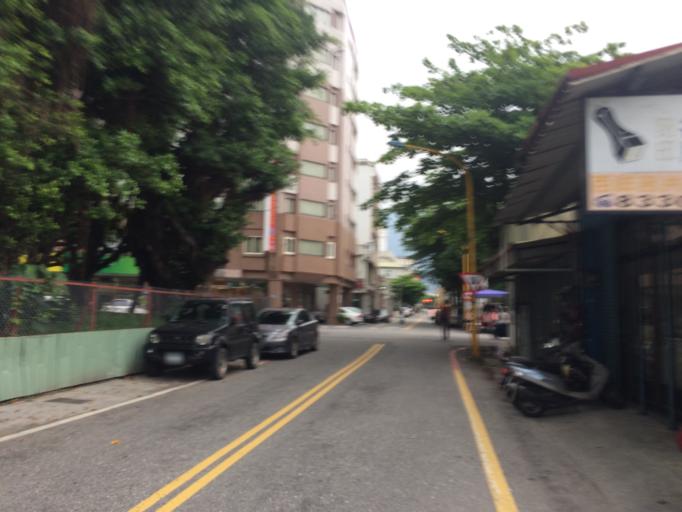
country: TW
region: Taiwan
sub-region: Hualien
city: Hualian
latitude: 23.9805
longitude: 121.6087
